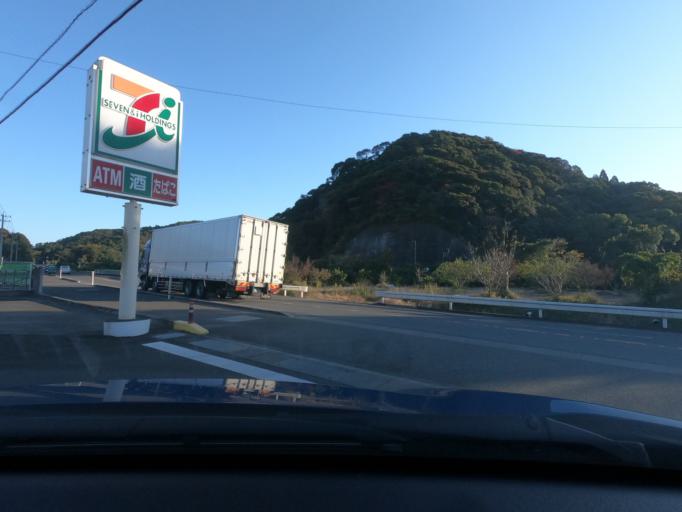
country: JP
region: Kagoshima
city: Satsumasendai
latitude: 31.8467
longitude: 130.2718
